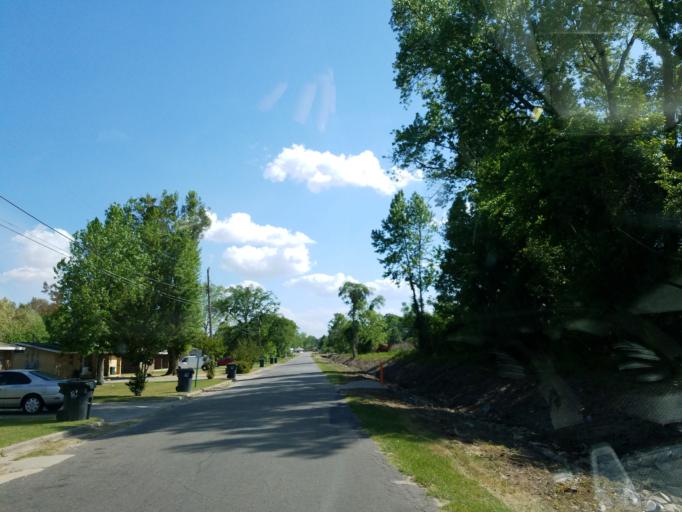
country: US
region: Georgia
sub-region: Dooly County
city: Unadilla
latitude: 32.1991
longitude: -83.7598
